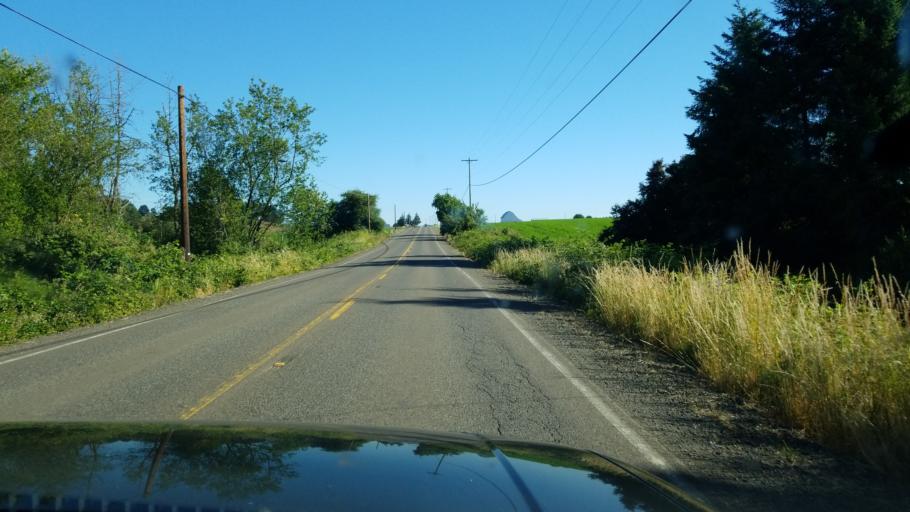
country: US
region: Oregon
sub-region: Yamhill County
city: Carlton
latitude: 45.2788
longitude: -123.2035
